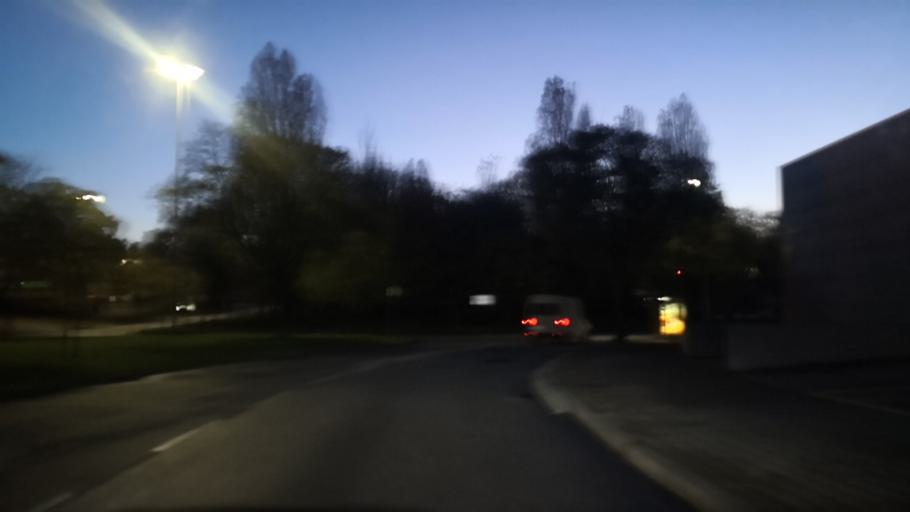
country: PT
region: Porto
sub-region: Matosinhos
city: Senhora da Hora
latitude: 41.1707
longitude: -8.6424
